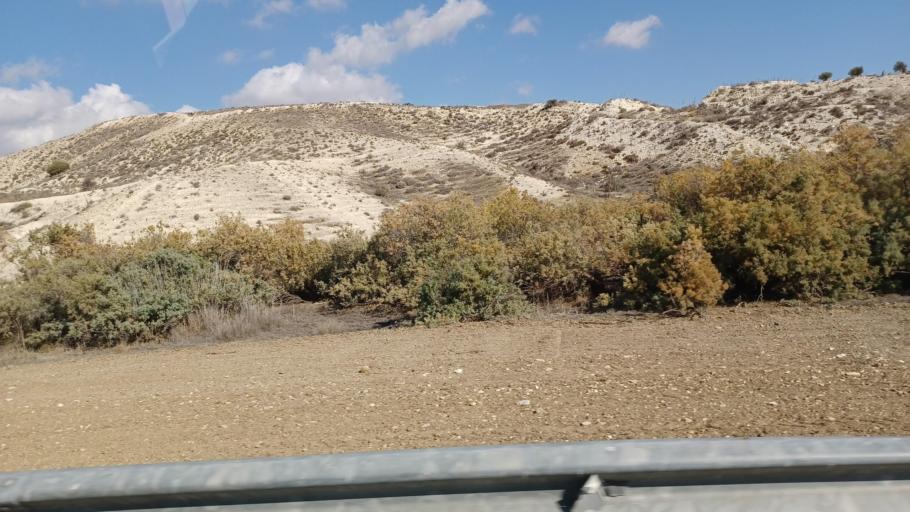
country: CY
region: Larnaka
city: Voroklini
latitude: 35.0081
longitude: 33.6463
